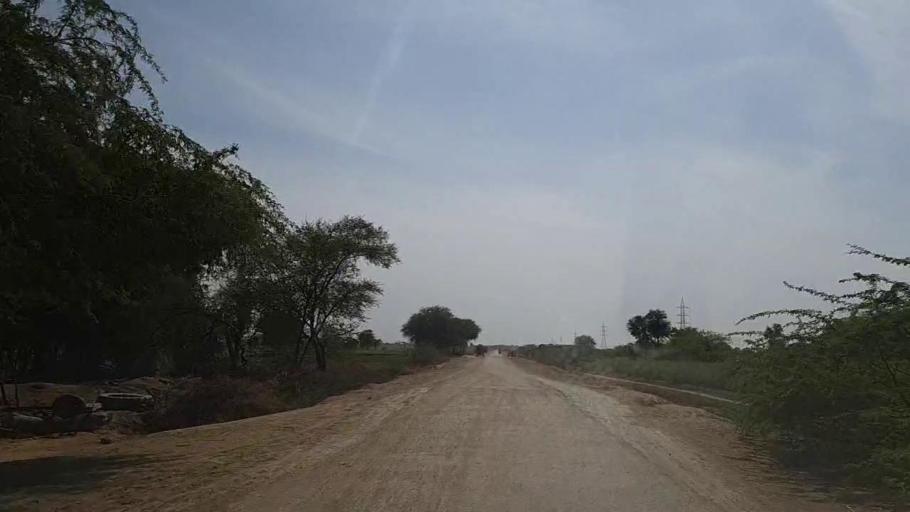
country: PK
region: Sindh
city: Kunri
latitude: 25.1805
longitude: 69.4581
